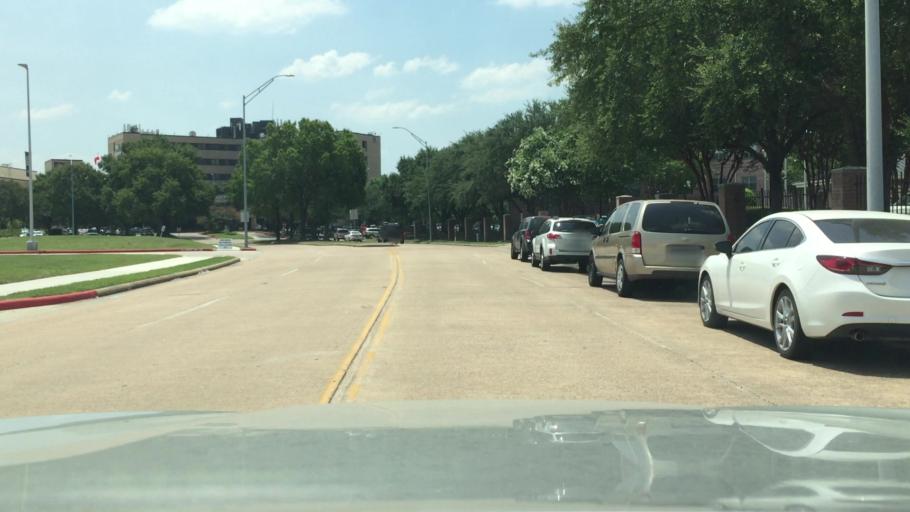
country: US
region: Texas
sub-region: Harris County
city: Bunker Hill Village
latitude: 29.7317
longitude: -95.5953
